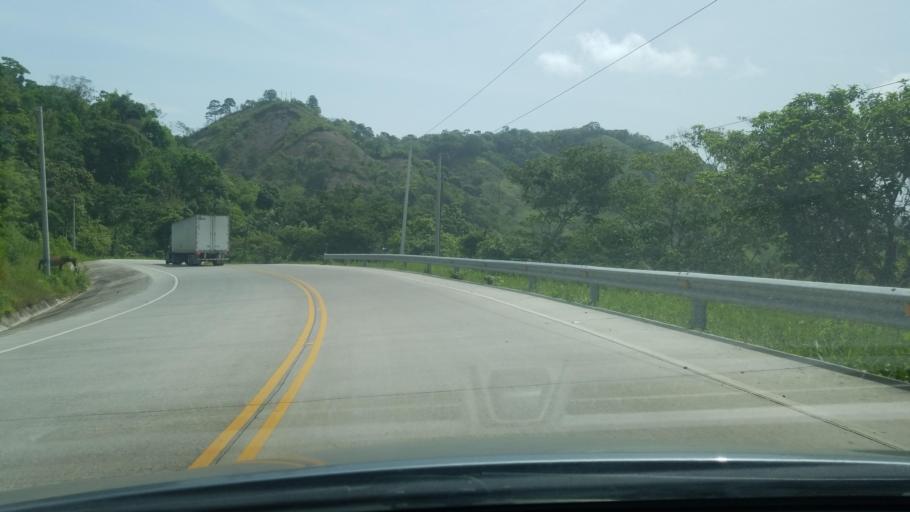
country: HN
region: Copan
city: San Jeronimo
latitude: 14.9593
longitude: -88.8959
